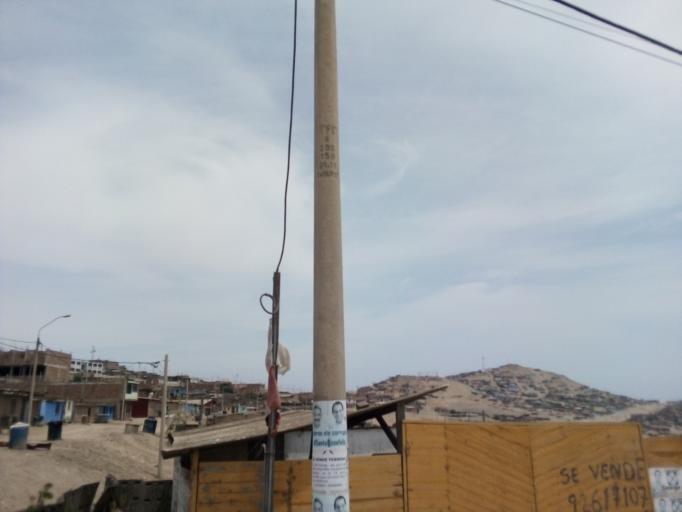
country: PE
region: Lima
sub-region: Lima
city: Santa Rosa
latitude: -11.8182
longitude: -77.1622
